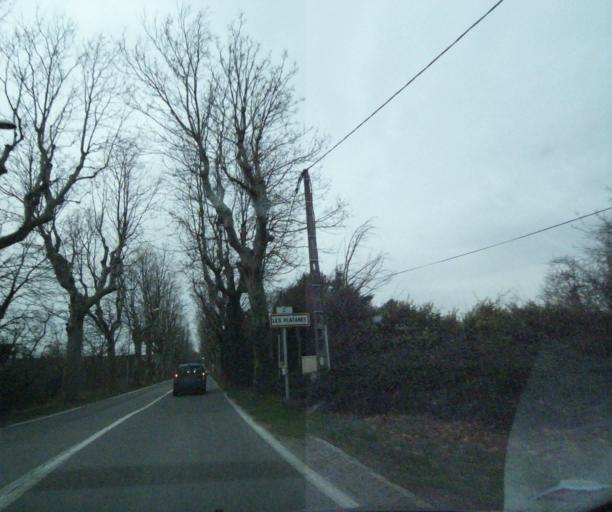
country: FR
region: Provence-Alpes-Cote d'Azur
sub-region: Departement des Bouches-du-Rhone
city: Aix-en-Provence
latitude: 43.5636
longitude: 5.4635
